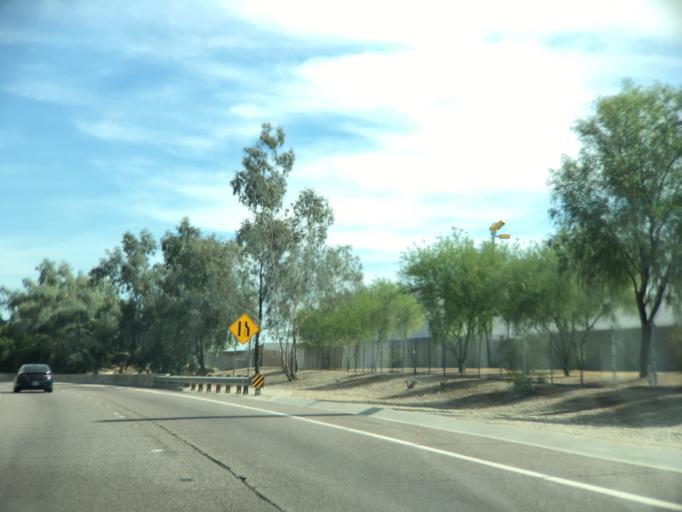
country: US
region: Arizona
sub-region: Maricopa County
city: Tolleson
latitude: 33.4608
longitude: -112.2713
